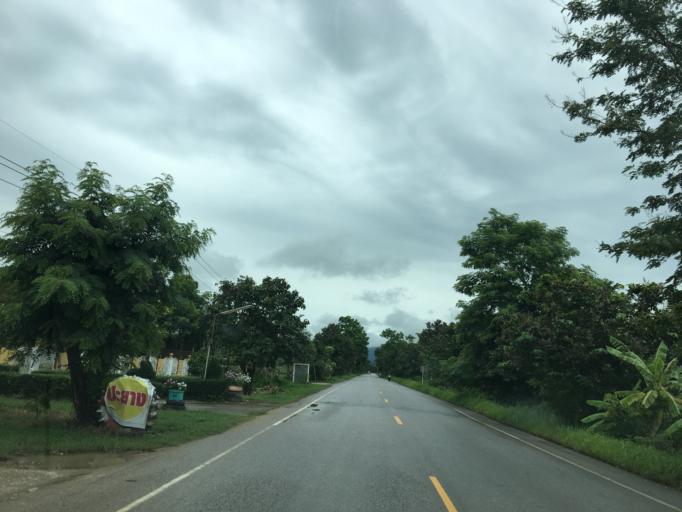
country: TH
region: Chiang Rai
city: Pa Daet
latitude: 19.4978
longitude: 99.9764
